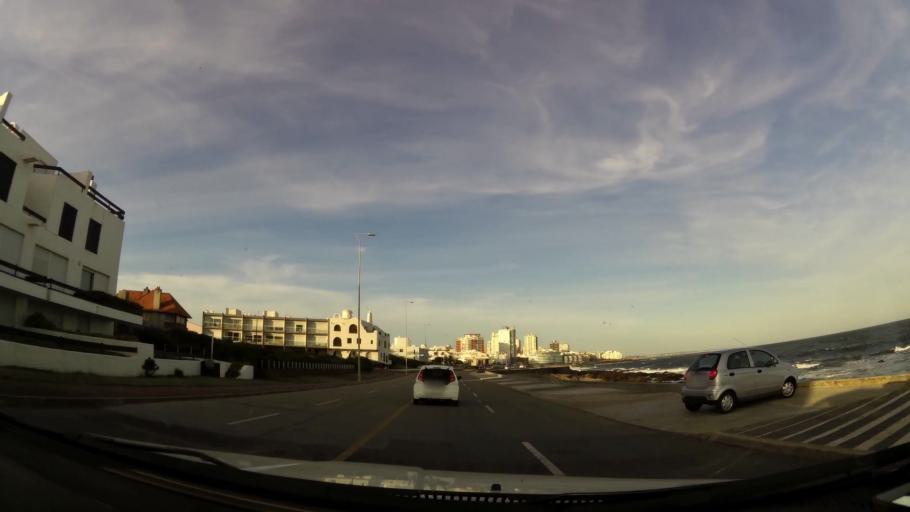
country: UY
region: Maldonado
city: Punta del Este
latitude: -34.9726
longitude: -54.9513
